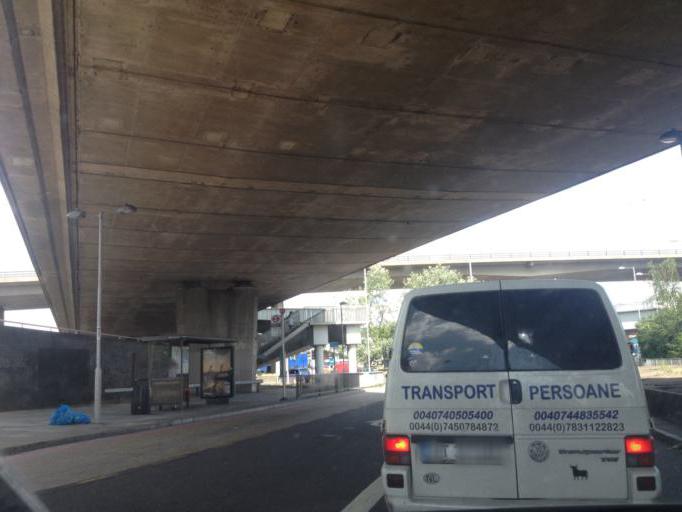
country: GB
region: England
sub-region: Greater London
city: Hendon
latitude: 51.5702
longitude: -0.2316
